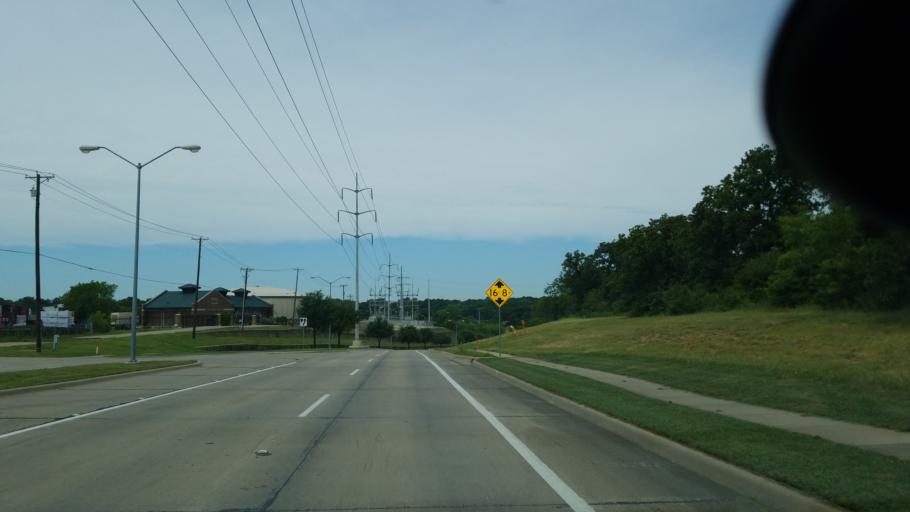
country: US
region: Texas
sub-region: Dallas County
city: Irving
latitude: 32.8440
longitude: -96.9310
